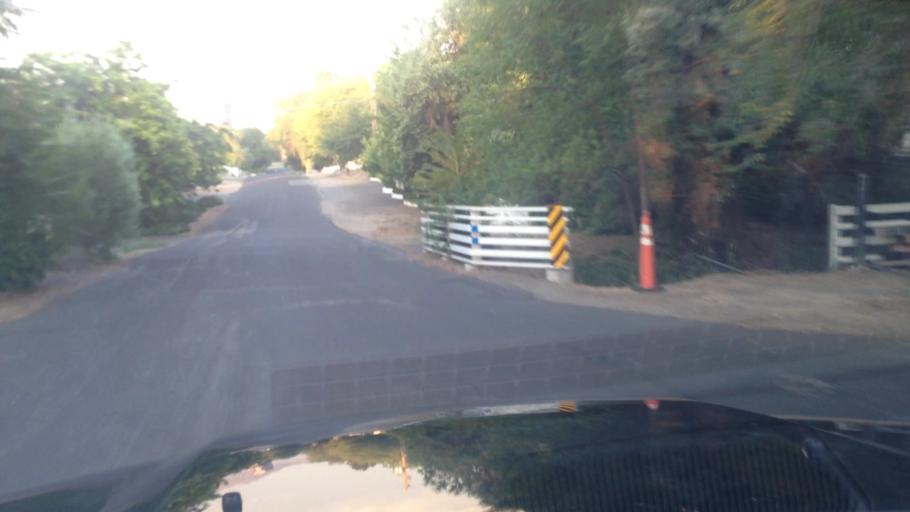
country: US
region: Nevada
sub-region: Washoe County
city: Reno
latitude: 39.4883
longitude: -119.8173
